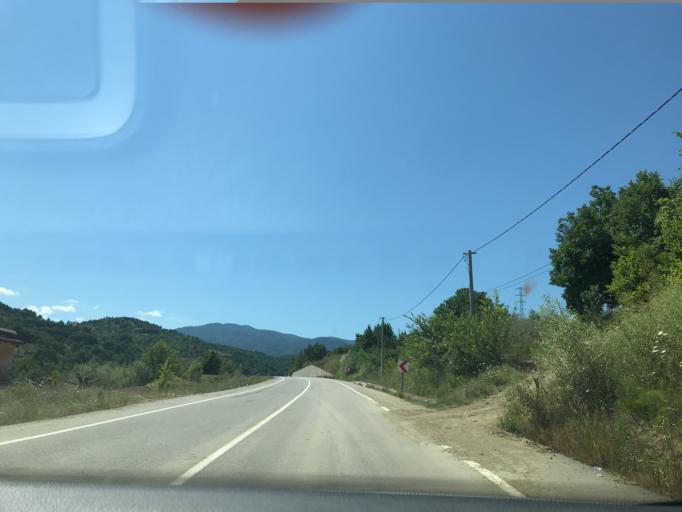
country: TR
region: Bursa
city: Tahtakopru
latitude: 39.9763
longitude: 29.6045
